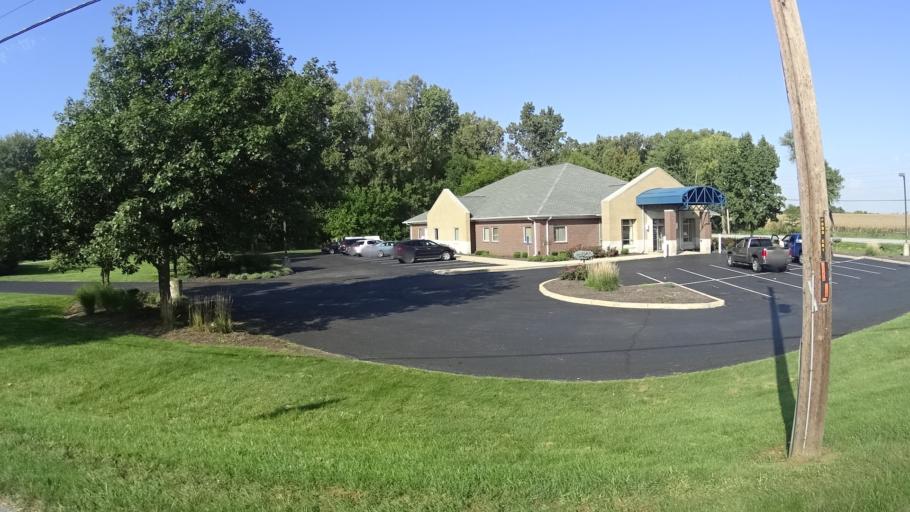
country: US
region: Indiana
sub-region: Madison County
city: Lapel
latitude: 40.0764
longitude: -85.8488
